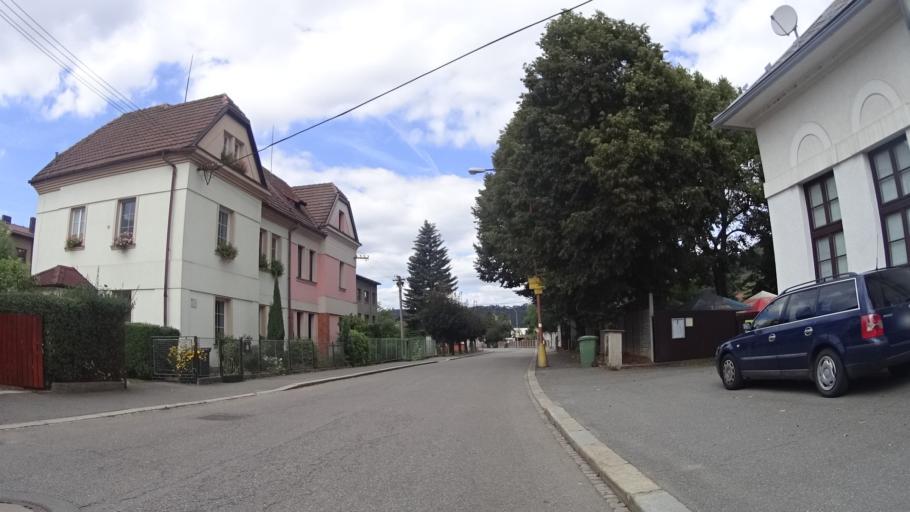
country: CZ
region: Pardubicky
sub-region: Okres Usti nad Orlici
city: Usti nad Orlici
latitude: 49.9704
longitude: 16.3678
